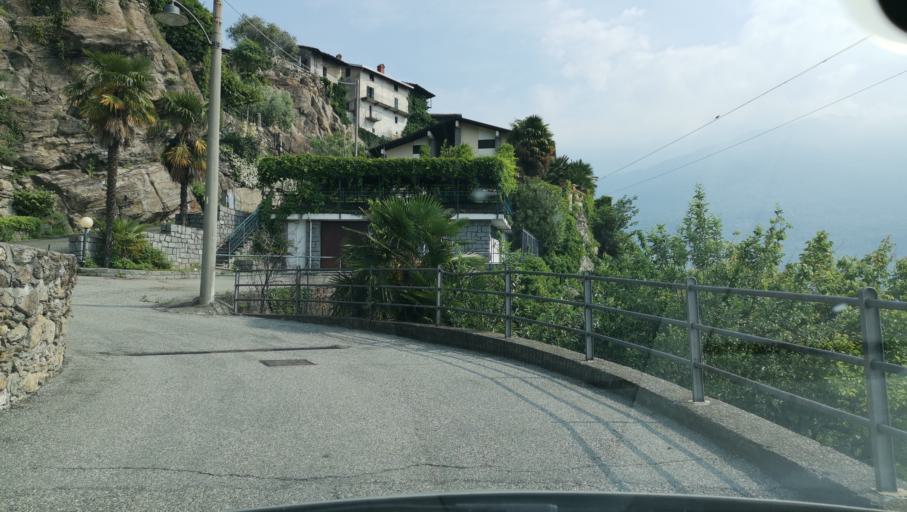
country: IT
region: Piedmont
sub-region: Provincia di Torino
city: Quassolo
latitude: 45.5245
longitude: 7.8314
